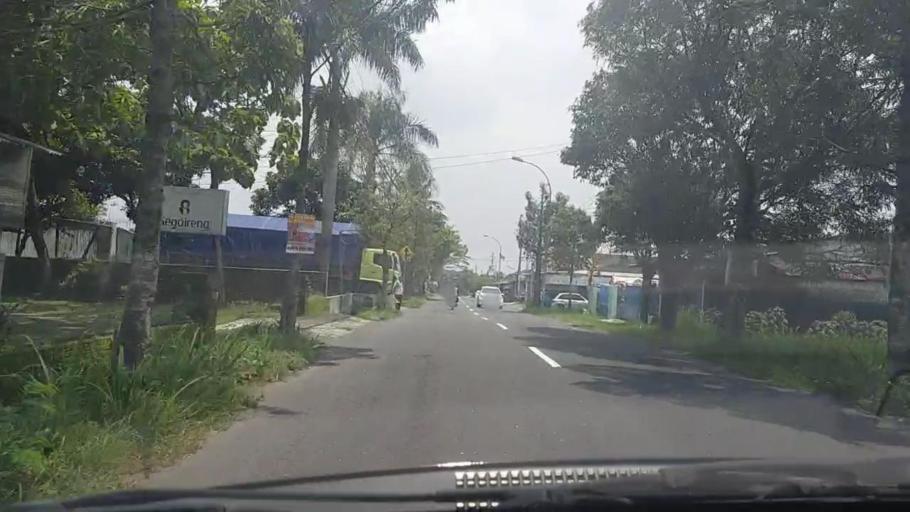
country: ID
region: Daerah Istimewa Yogyakarta
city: Sleman
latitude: -7.7013
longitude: 110.3871
